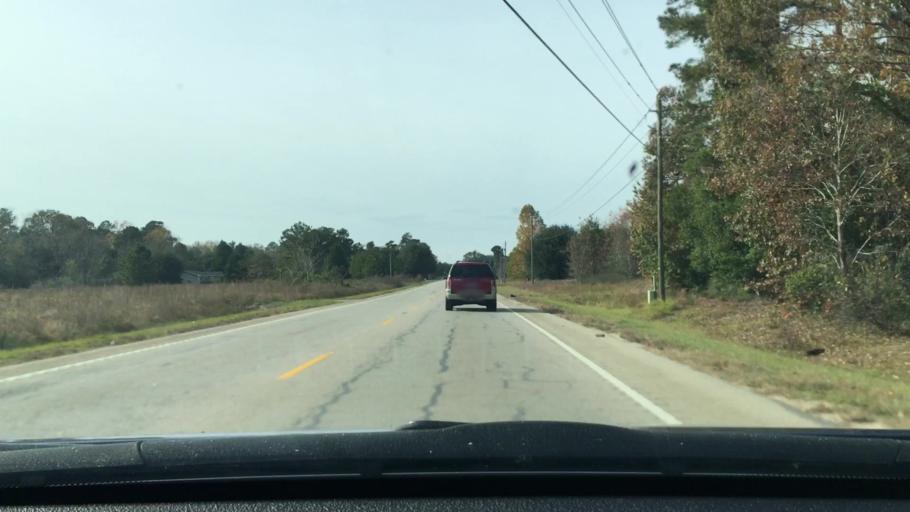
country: US
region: South Carolina
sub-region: Sumter County
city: Cherryvale
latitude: 33.9372
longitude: -80.4639
